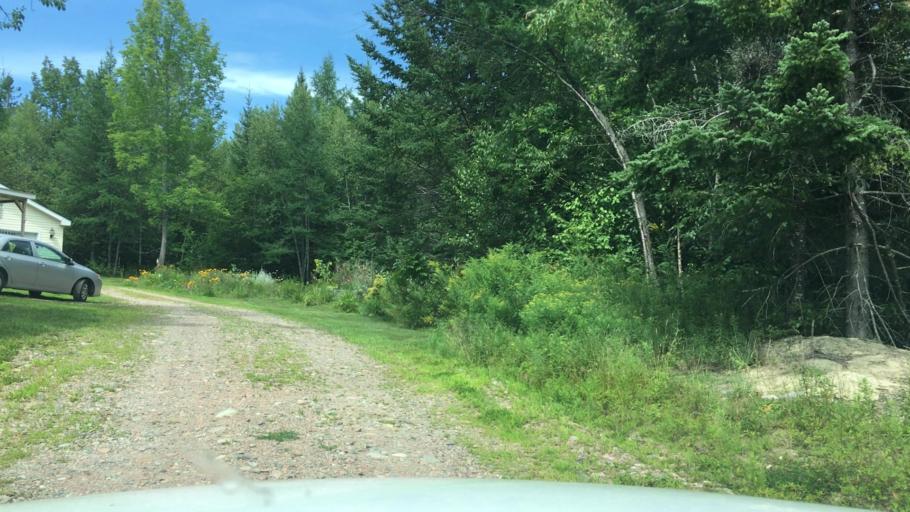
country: CA
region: New Brunswick
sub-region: Charlotte County
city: Saint Andrews
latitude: 45.0365
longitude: -67.1165
